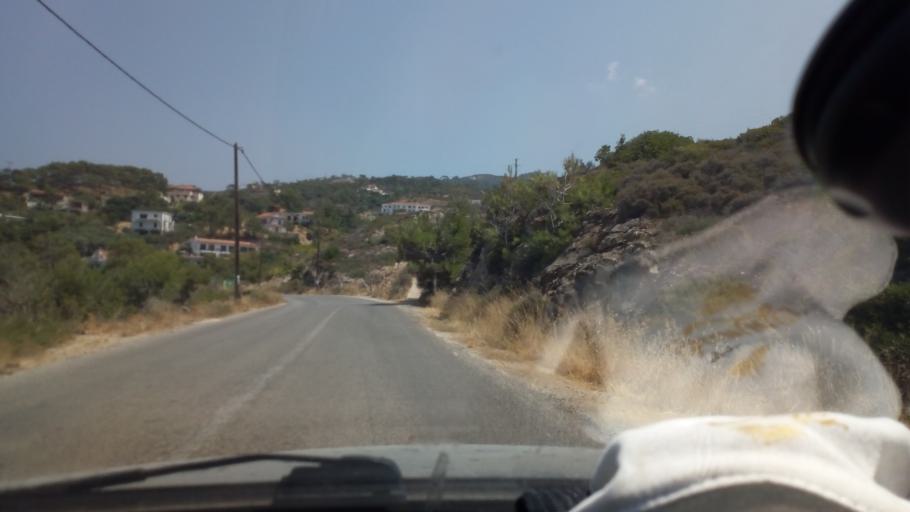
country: GR
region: North Aegean
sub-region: Nomos Samou
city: Agios Kirykos
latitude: 37.6294
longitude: 26.1003
